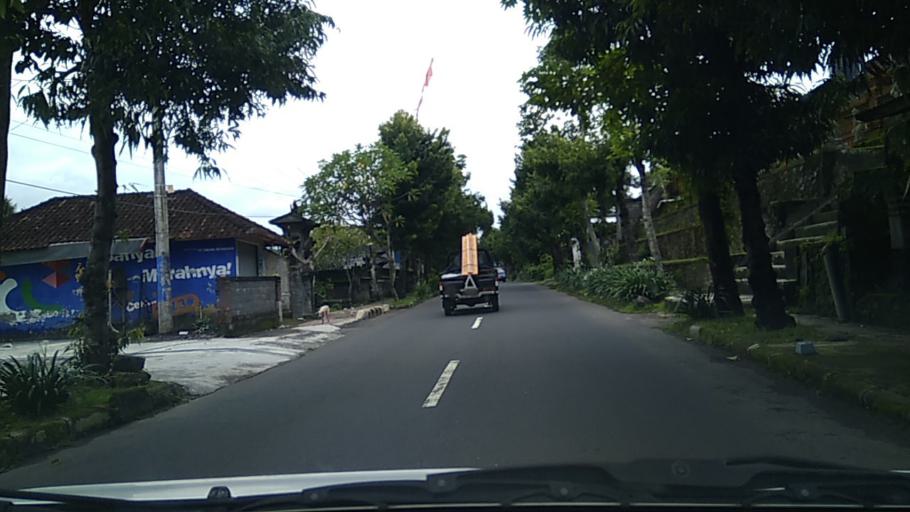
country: ID
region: Bali
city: Banjar Kelodan
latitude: -8.5343
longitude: 115.3479
